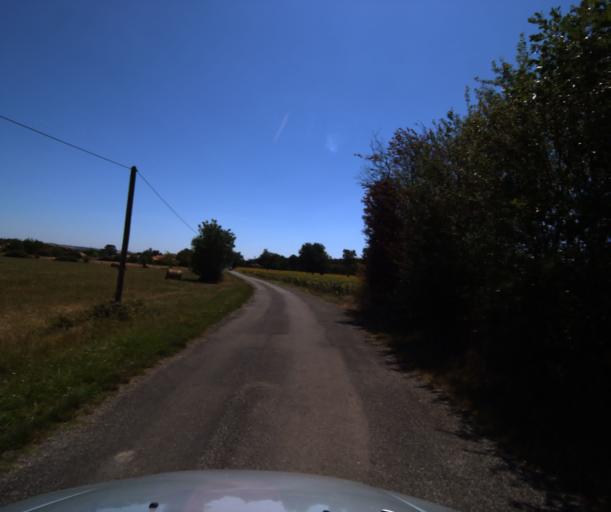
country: FR
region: Midi-Pyrenees
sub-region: Departement de la Haute-Garonne
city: Muret
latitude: 43.4538
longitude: 1.3474
